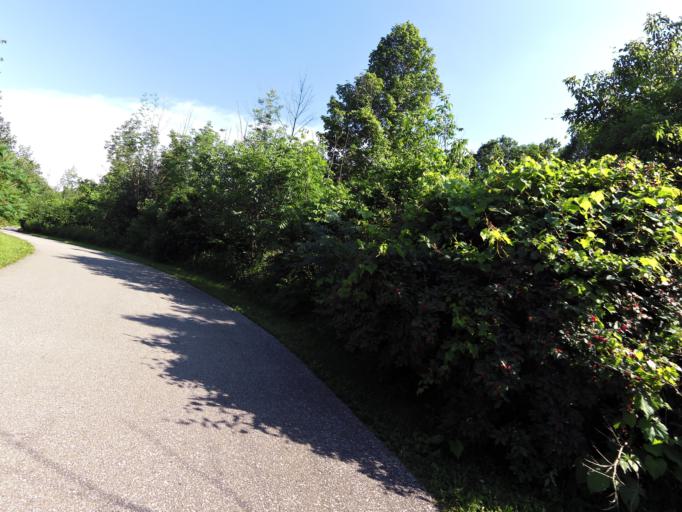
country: CA
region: Ontario
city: Etobicoke
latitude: 43.7286
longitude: -79.5600
